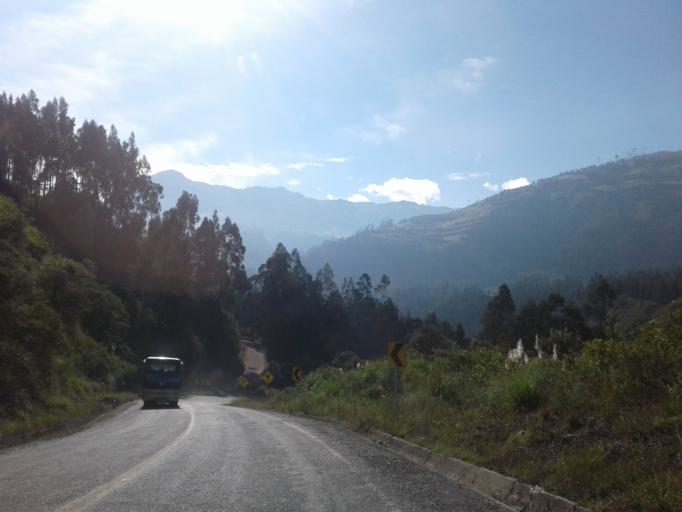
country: EC
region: Tungurahua
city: Banos
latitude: -1.5197
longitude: -78.5090
